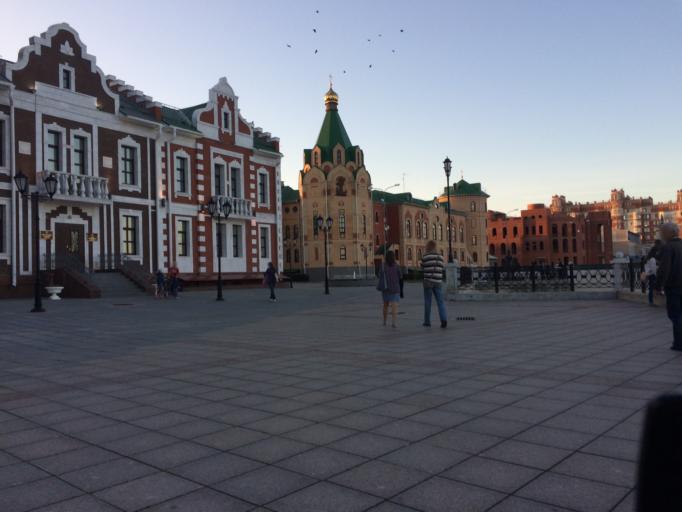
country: RU
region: Mariy-El
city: Yoshkar-Ola
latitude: 56.6311
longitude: 47.8992
